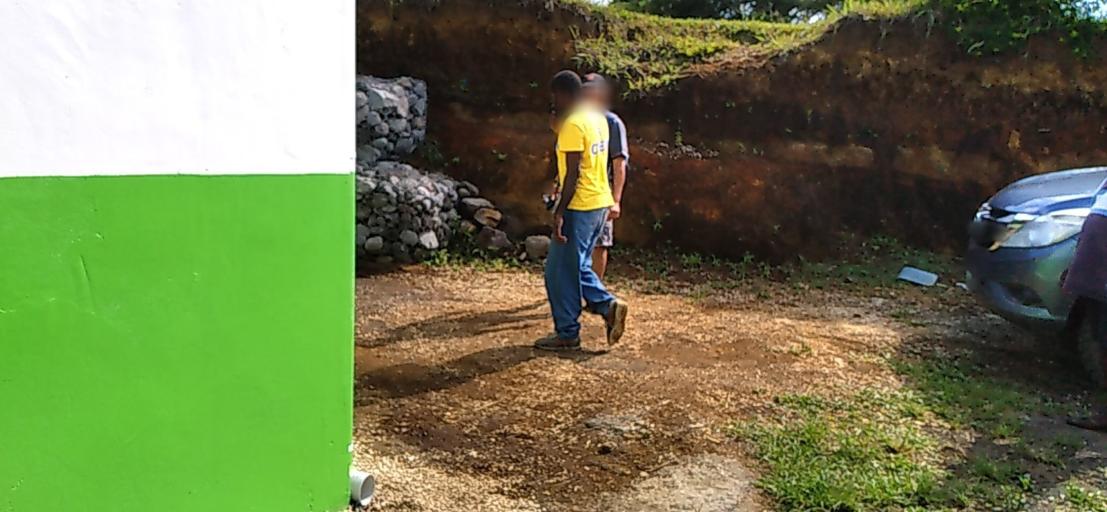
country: VU
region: Shefa
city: Port-Vila
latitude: -16.9001
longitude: 168.5731
